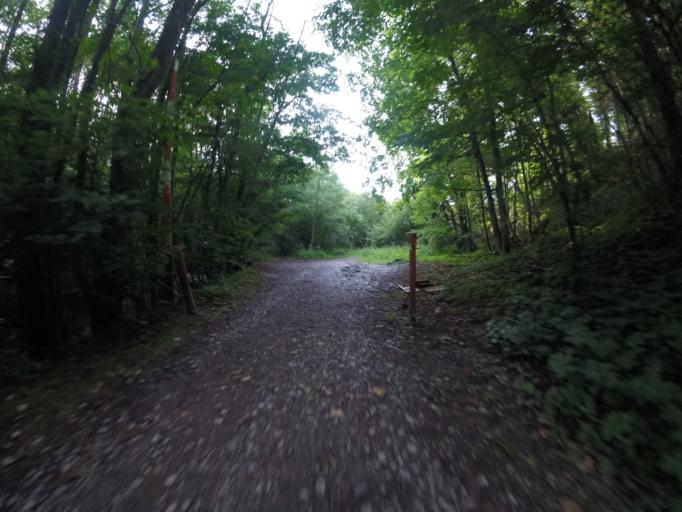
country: DE
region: Baden-Wuerttemberg
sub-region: Regierungsbezirk Stuttgart
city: Mittelschontal
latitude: 48.9344
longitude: 9.4060
